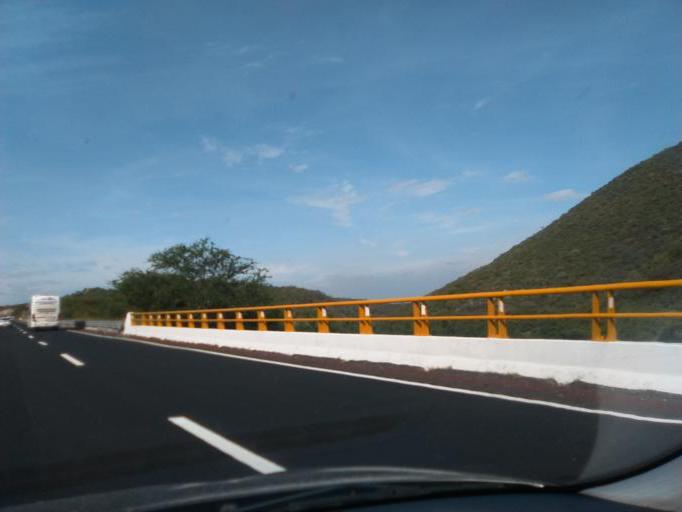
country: MX
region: Morelos
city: Tilzapotla
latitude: 18.4544
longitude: -99.1726
